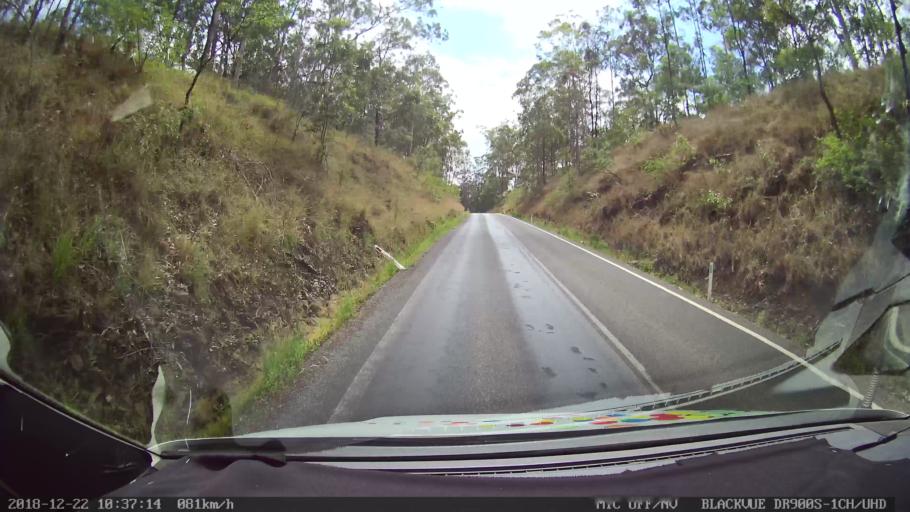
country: AU
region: New South Wales
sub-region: Clarence Valley
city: South Grafton
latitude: -29.6333
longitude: 152.7030
